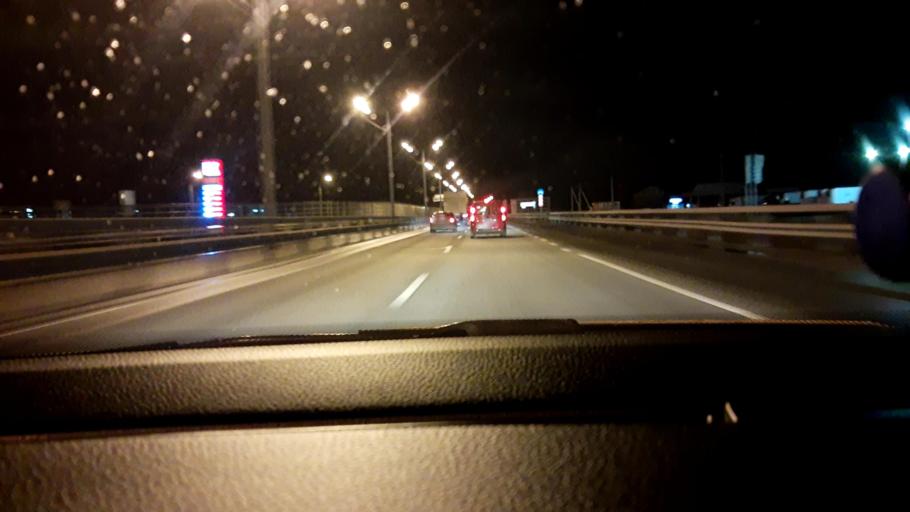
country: RU
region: Moskovskaya
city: Demikhovo
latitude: 55.8583
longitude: 38.8866
